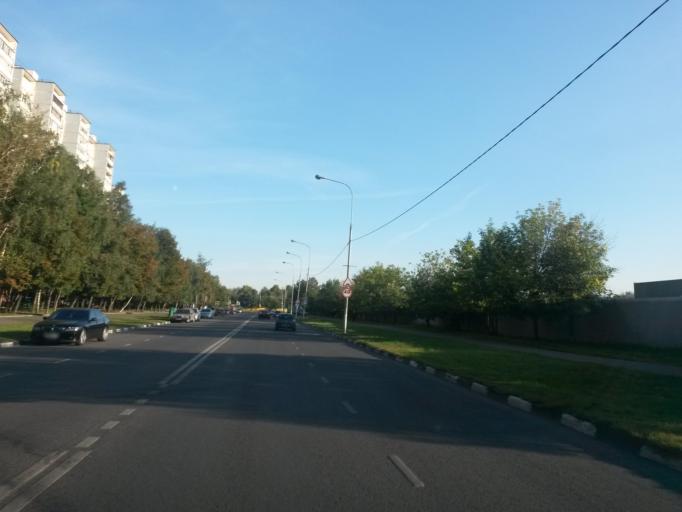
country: RU
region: Moscow
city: Orekhovo-Borisovo
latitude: 55.6050
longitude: 37.7253
